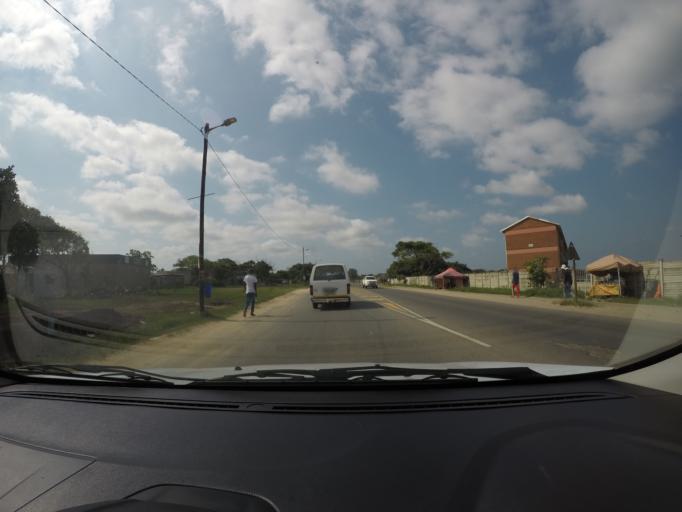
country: ZA
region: KwaZulu-Natal
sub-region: uThungulu District Municipality
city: eSikhawini
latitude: -28.8743
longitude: 31.9016
